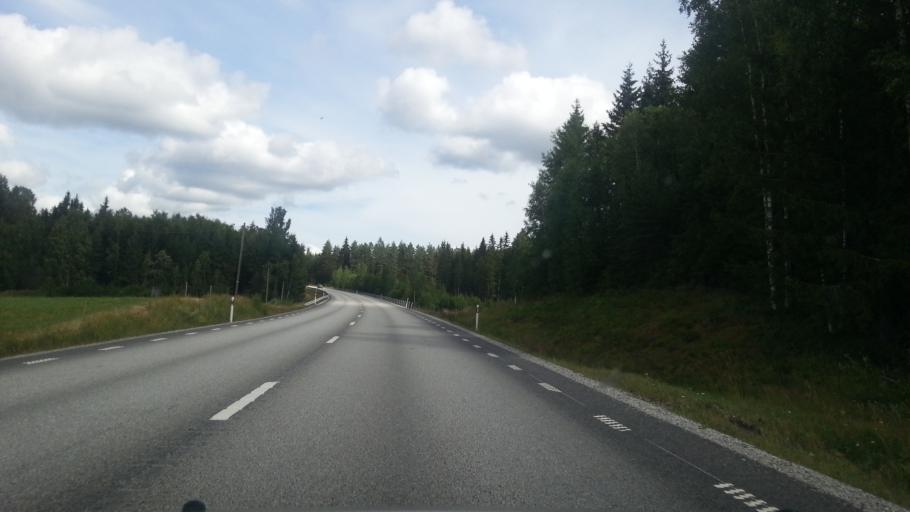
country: SE
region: Vaestmanland
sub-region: Skinnskattebergs Kommun
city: Skinnskatteberg
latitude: 59.7528
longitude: 15.4483
